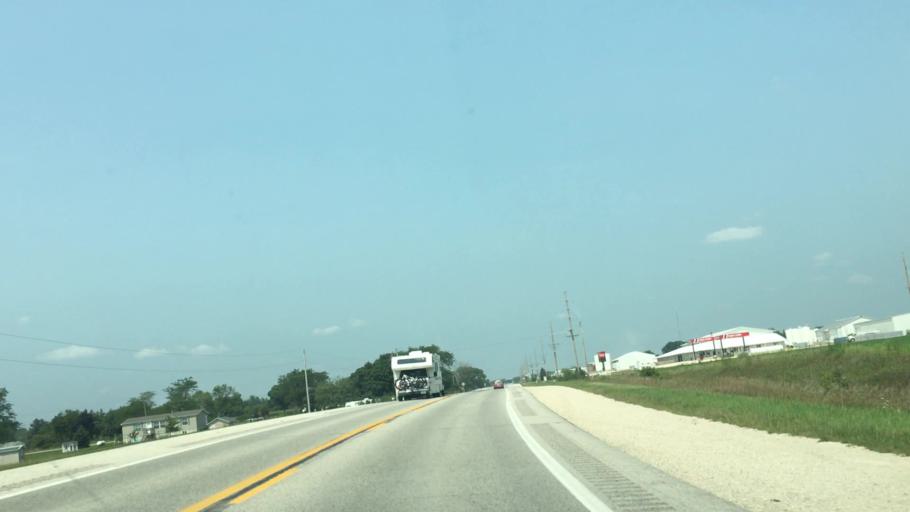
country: US
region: Iowa
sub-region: Fayette County
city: Oelwein
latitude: 42.6266
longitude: -91.9091
